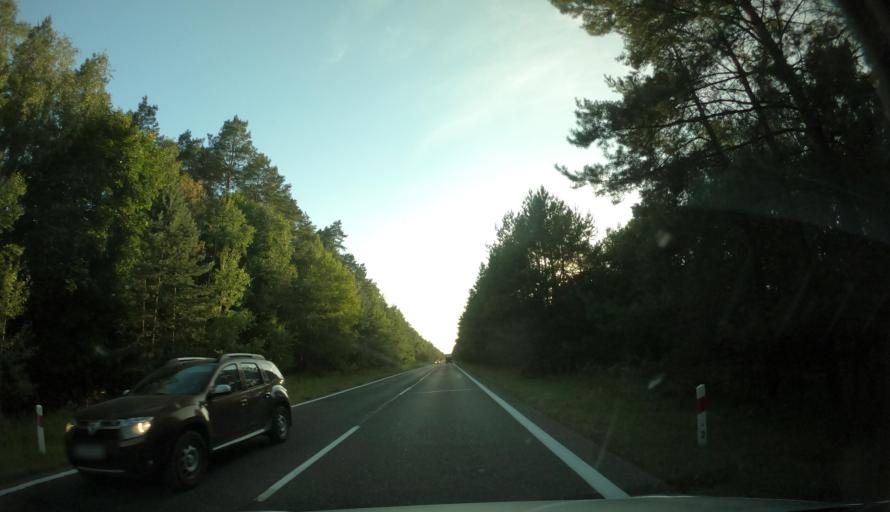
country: PL
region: Kujawsko-Pomorskie
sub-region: Powiat bydgoski
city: Koronowo
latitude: 53.3116
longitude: 18.0127
